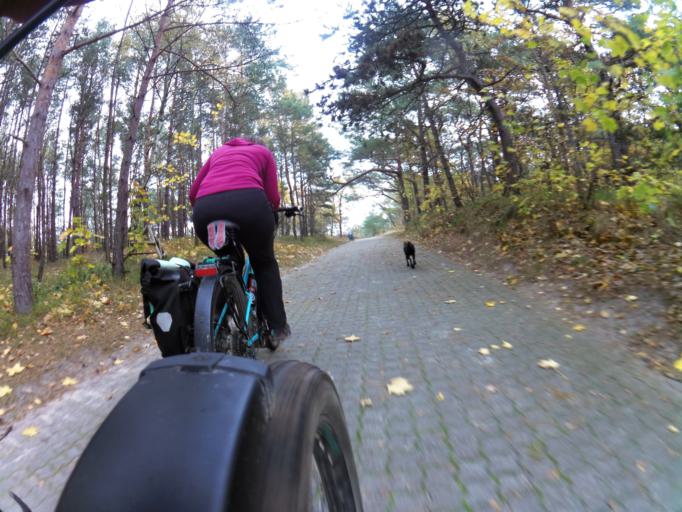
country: PL
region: Pomeranian Voivodeship
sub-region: Powiat pucki
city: Jastarnia
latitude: 54.6981
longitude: 18.6871
